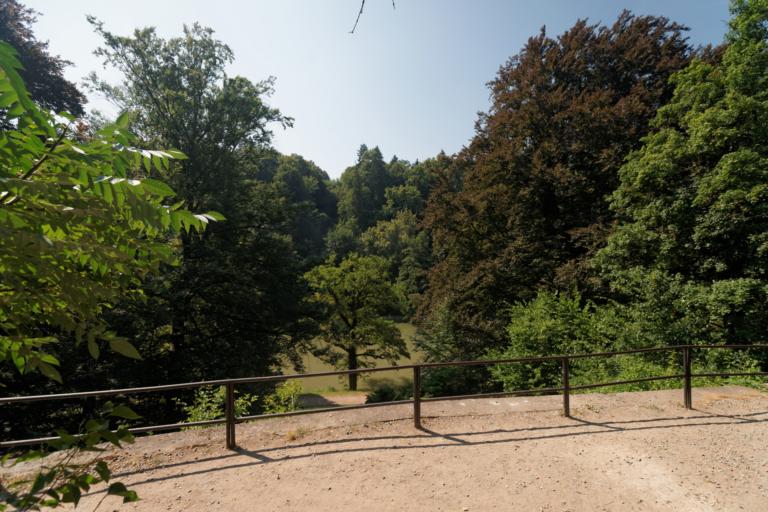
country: CZ
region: Kralovehradecky
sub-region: Okres Rychnov nad Kneznou
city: Opocno
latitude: 50.2643
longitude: 16.1155
